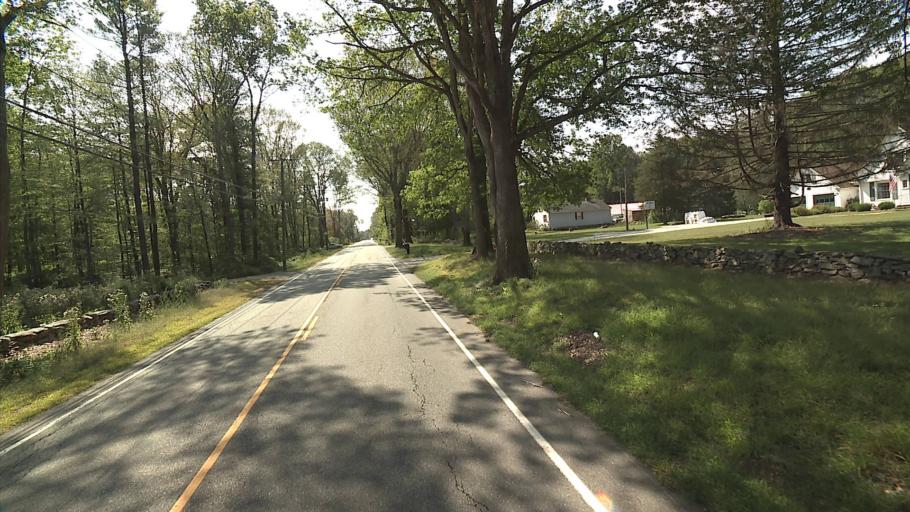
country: US
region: Connecticut
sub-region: Windham County
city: East Brooklyn
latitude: 41.8453
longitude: -71.9589
